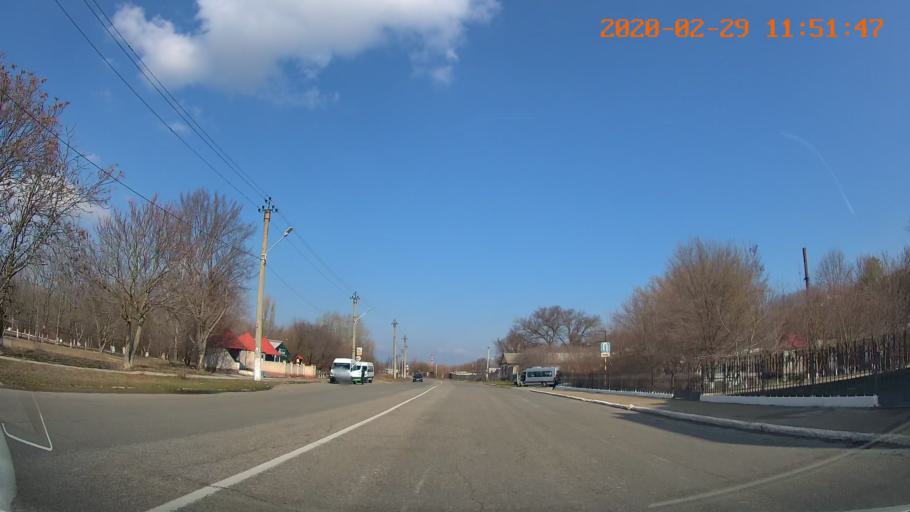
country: MD
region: Telenesti
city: Ribnita
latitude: 47.7667
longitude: 28.9907
